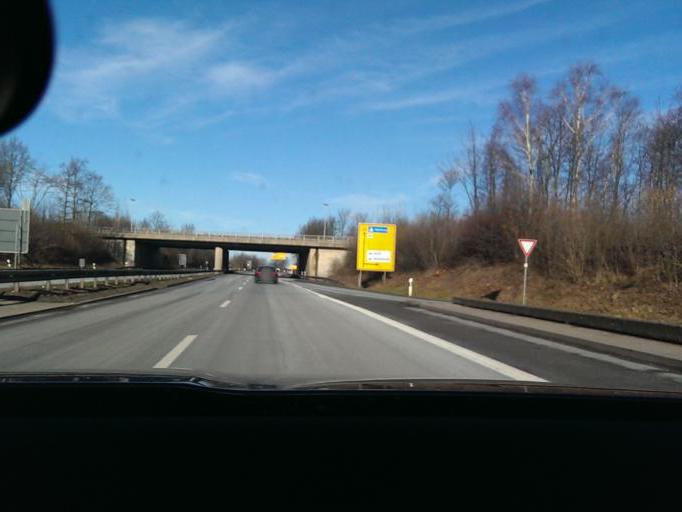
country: DE
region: Lower Saxony
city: Langenhagen
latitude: 52.4393
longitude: 9.7218
